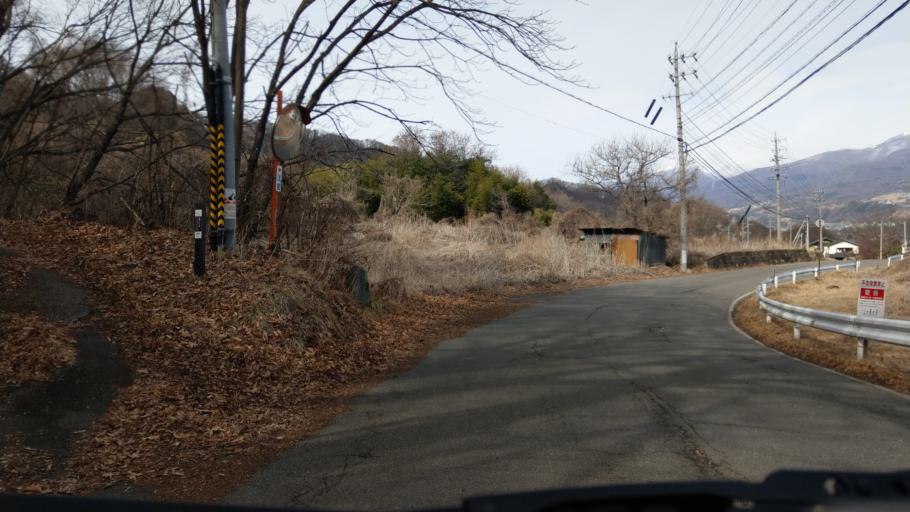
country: JP
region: Nagano
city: Komoro
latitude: 36.3024
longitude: 138.4168
